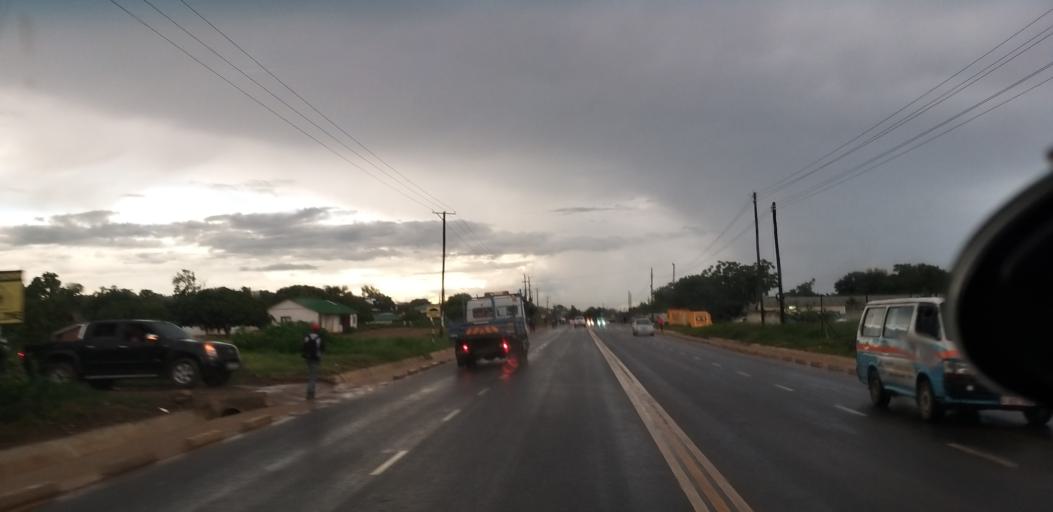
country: ZM
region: Lusaka
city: Lusaka
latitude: -15.4256
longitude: 28.3565
